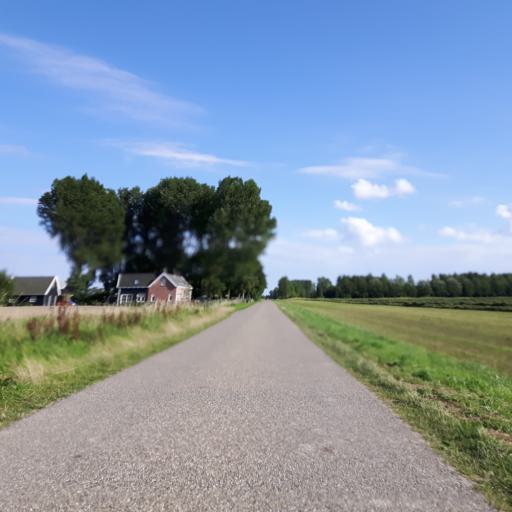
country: NL
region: Zeeland
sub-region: Gemeente Goes
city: Goes
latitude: 51.5297
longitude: 3.9164
